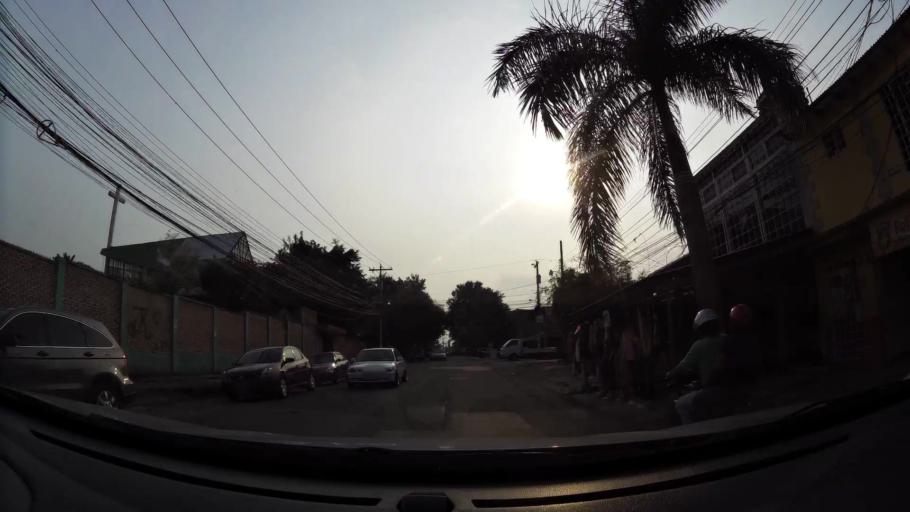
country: HN
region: Francisco Morazan
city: Tegucigalpa
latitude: 14.0657
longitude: -87.1813
